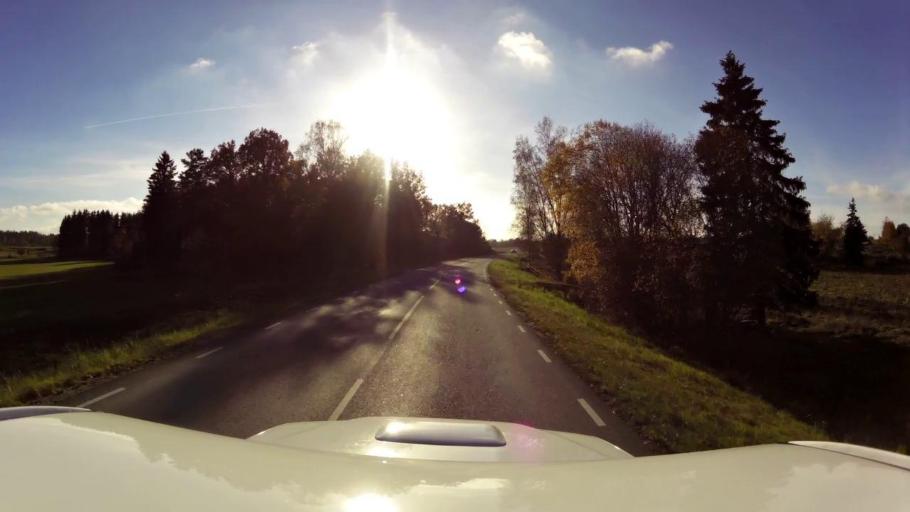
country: SE
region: OEstergoetland
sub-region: Linkopings Kommun
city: Vikingstad
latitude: 58.3071
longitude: 15.4888
